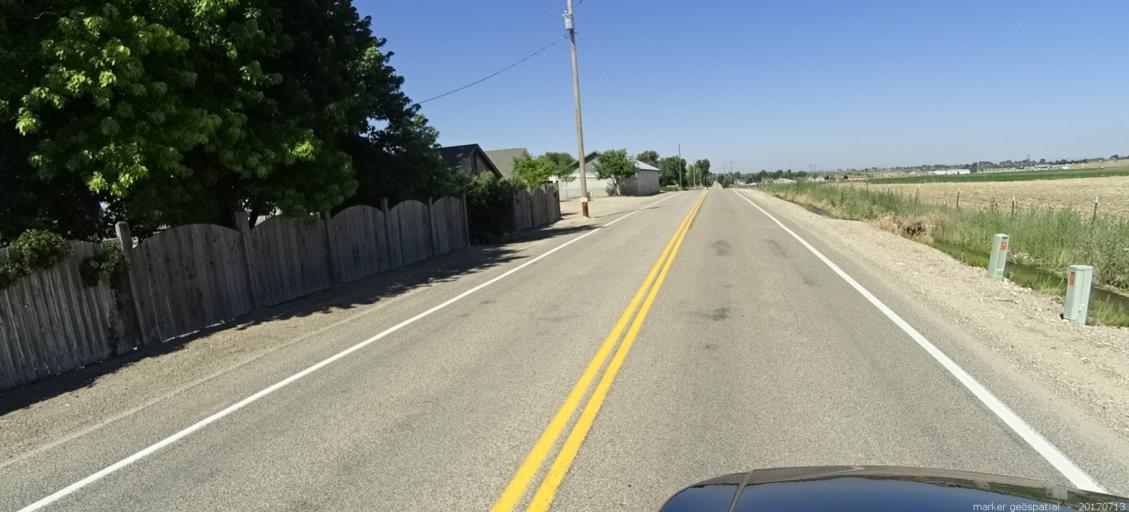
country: US
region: Idaho
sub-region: Ada County
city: Kuna
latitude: 43.5319
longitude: -116.3778
